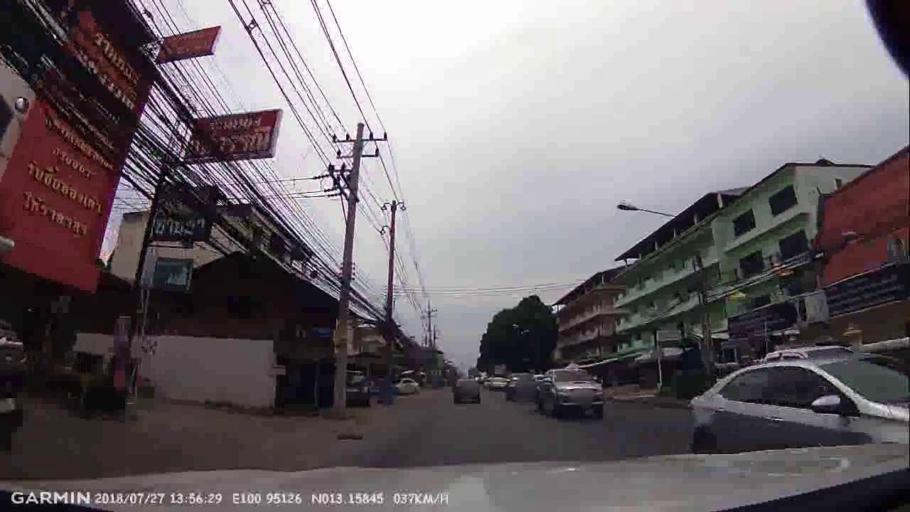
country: TH
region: Chon Buri
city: Si Racha
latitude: 13.1585
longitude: 100.9512
